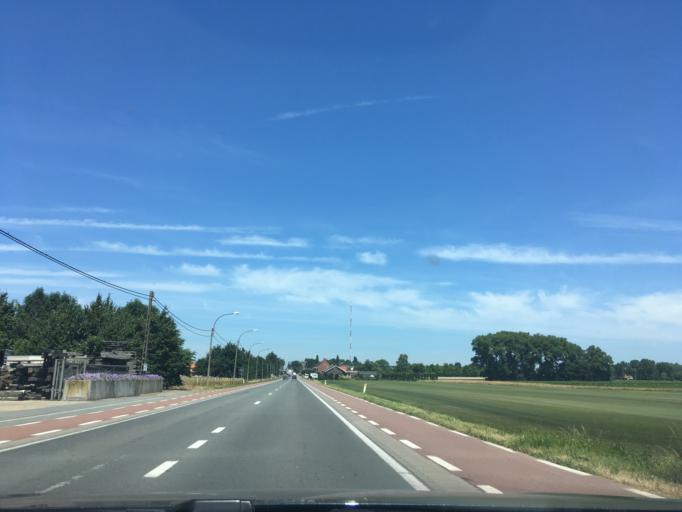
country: BE
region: Flanders
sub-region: Provincie West-Vlaanderen
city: Pittem
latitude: 51.0007
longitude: 3.2367
